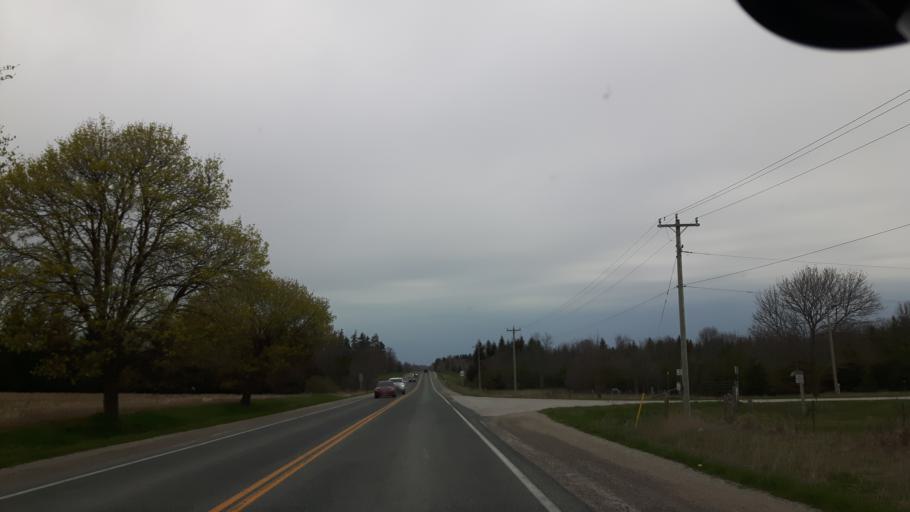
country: CA
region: Ontario
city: Bluewater
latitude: 43.6231
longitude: -81.5536
